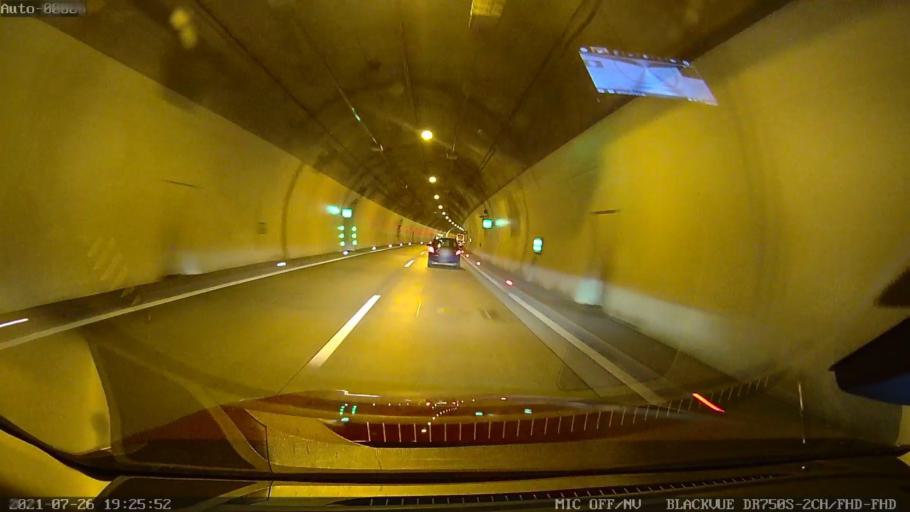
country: AT
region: Upper Austria
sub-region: Politischer Bezirk Kirchdorf an der Krems
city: Micheldorf in Oberoesterreich
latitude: 47.8599
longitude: 14.1539
